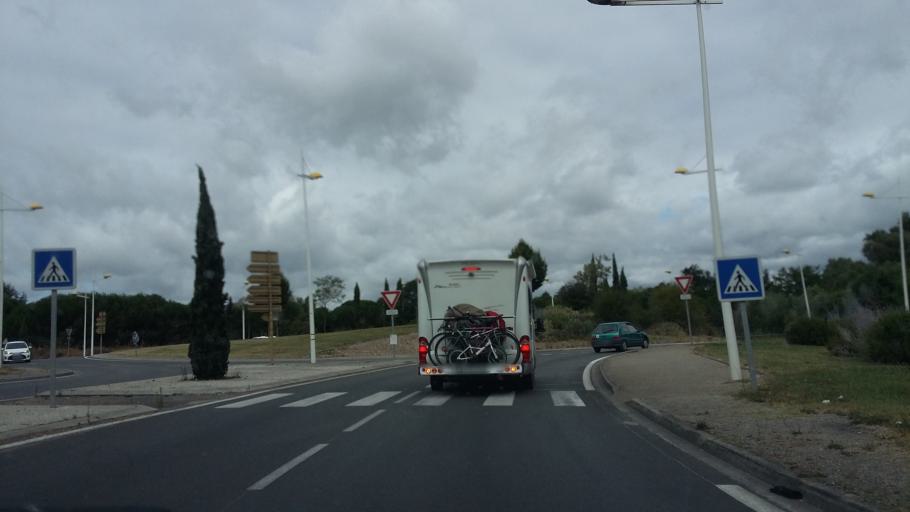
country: FR
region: Poitou-Charentes
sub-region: Departement de la Charente
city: Saint-Michel
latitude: 45.6370
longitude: 0.1210
